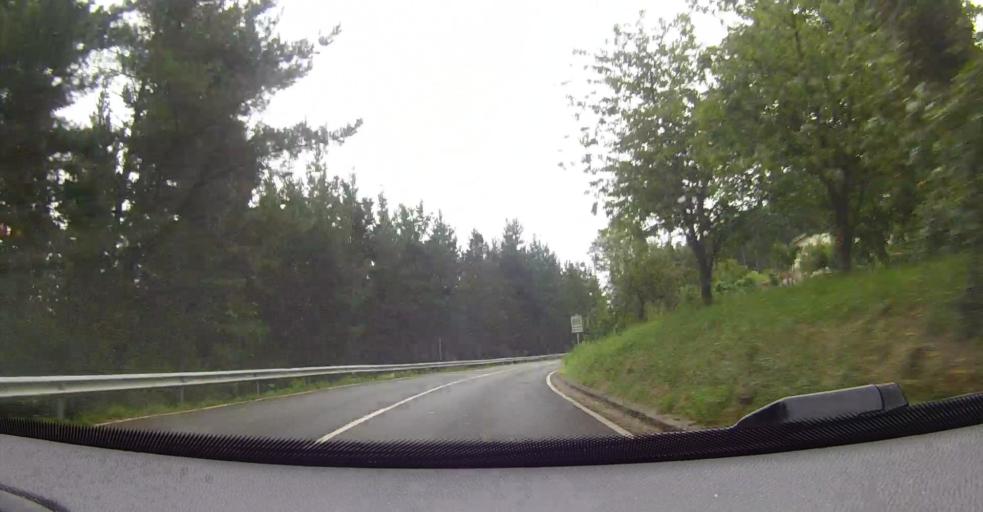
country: ES
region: Basque Country
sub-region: Bizkaia
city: Balmaseda
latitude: 43.2307
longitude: -3.1978
